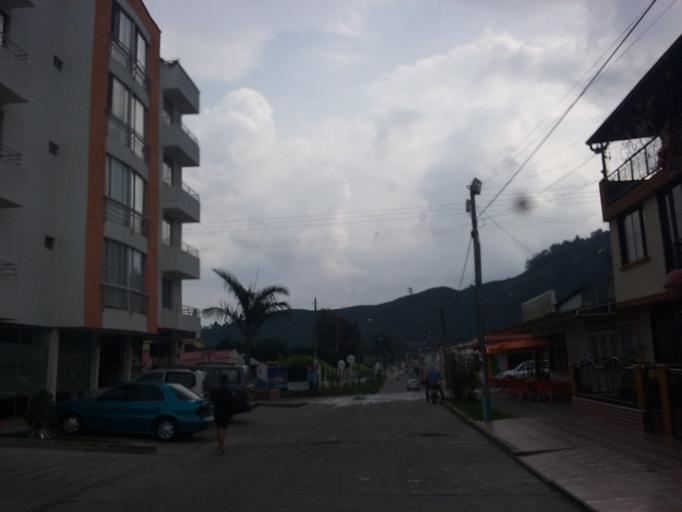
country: CO
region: Tolima
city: Libano
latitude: 4.9204
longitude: -75.0593
